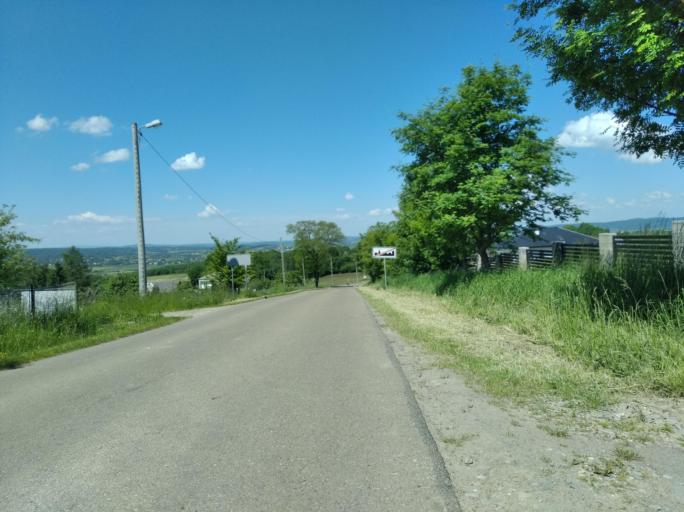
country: PL
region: Subcarpathian Voivodeship
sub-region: Powiat jasielski
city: Tarnowiec
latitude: 49.7215
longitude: 21.5977
